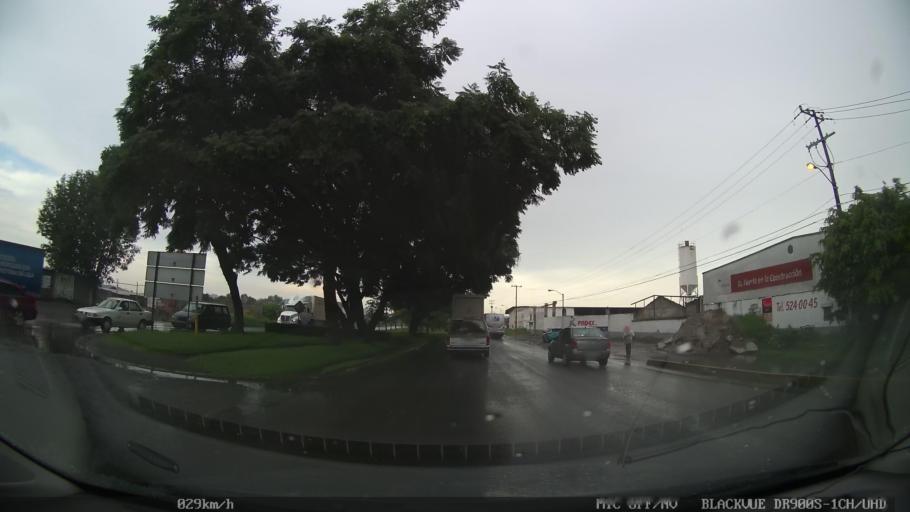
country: MX
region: Michoacan
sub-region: Uruapan
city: Toreo Bajo (El Toreo Bajo)
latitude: 19.4228
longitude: -102.0253
